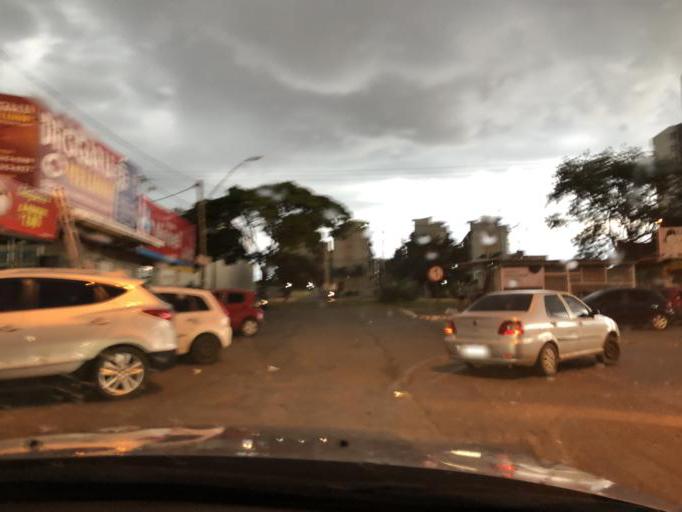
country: BR
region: Federal District
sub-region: Brasilia
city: Brasilia
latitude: -15.8131
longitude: -48.1030
